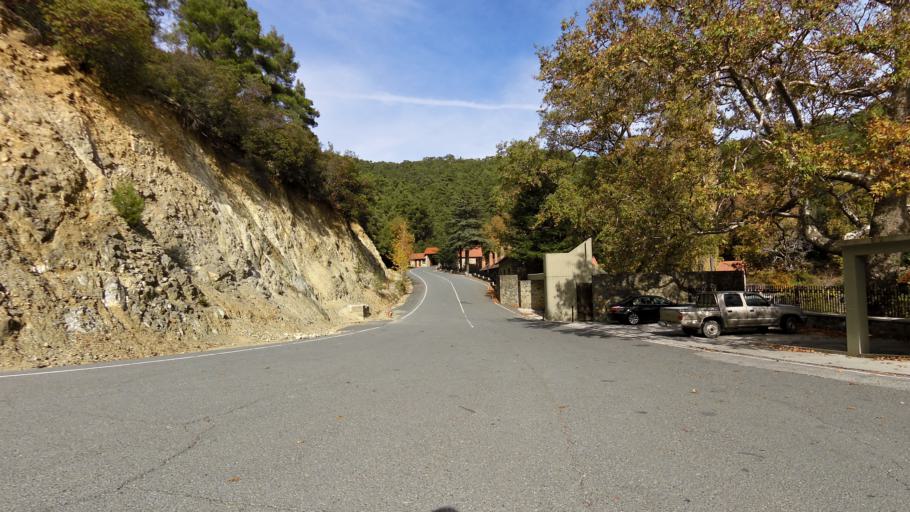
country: CY
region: Lefkosia
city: Kakopetria
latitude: 34.9119
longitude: 32.8378
